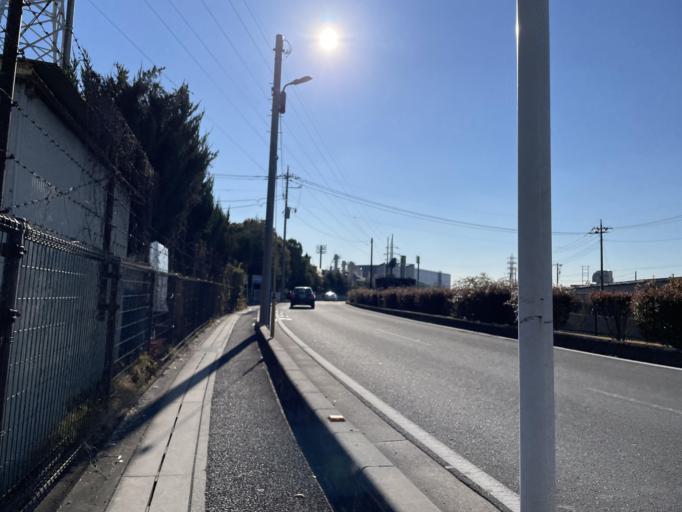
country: JP
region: Saitama
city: Yashio-shi
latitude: 35.8415
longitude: 139.8213
